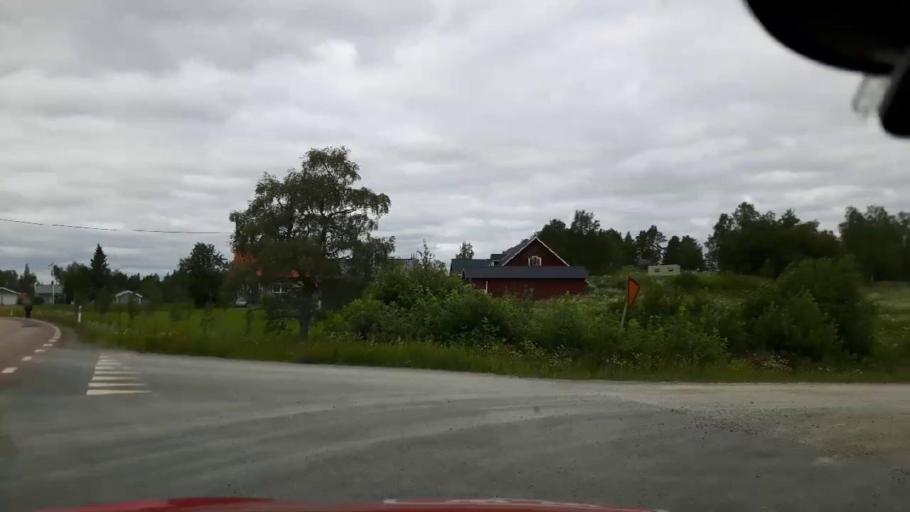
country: SE
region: Jaemtland
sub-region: OEstersunds Kommun
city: Brunflo
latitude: 63.0180
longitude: 14.9448
